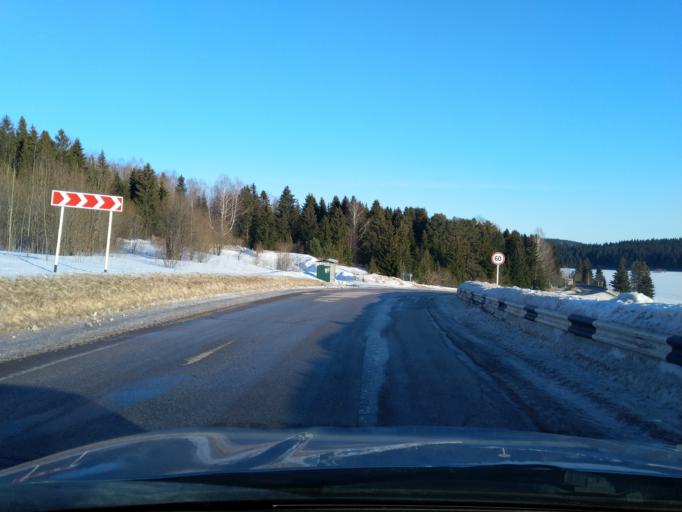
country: RU
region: Perm
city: Polazna
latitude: 58.3056
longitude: 56.4271
